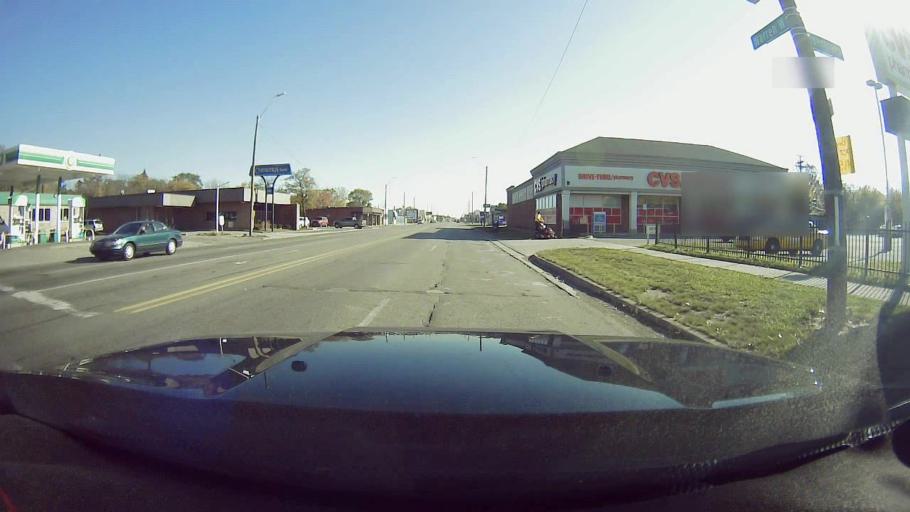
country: US
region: Michigan
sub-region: Wayne County
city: Dearborn Heights
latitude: 42.3431
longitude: -83.2352
